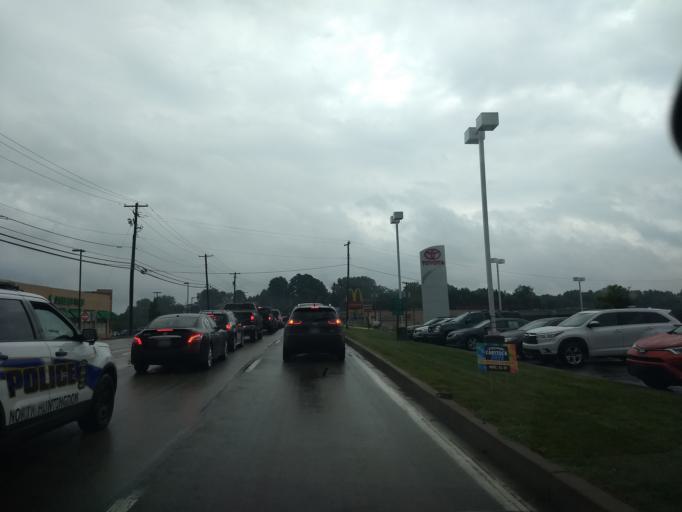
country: US
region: Pennsylvania
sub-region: Westmoreland County
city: Irwin
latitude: 40.3330
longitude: -79.7425
